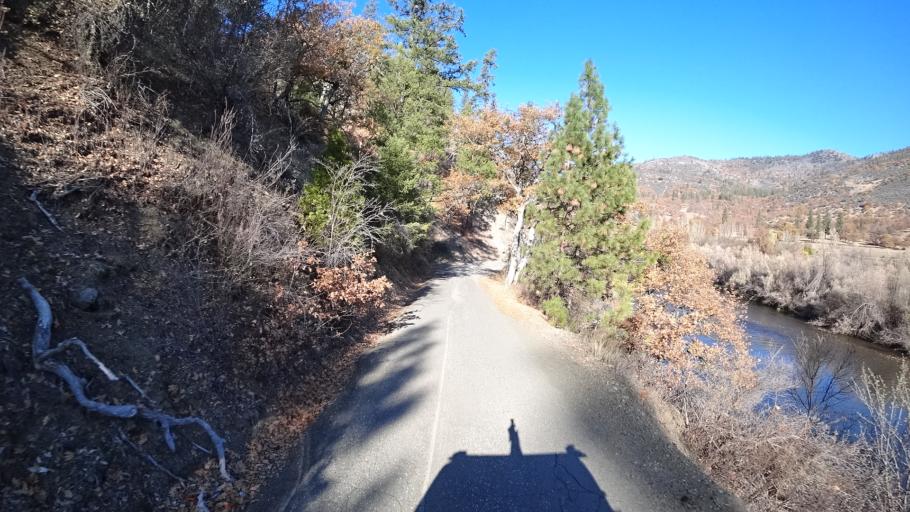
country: US
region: California
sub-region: Siskiyou County
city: Yreka
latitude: 41.8374
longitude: -122.8714
